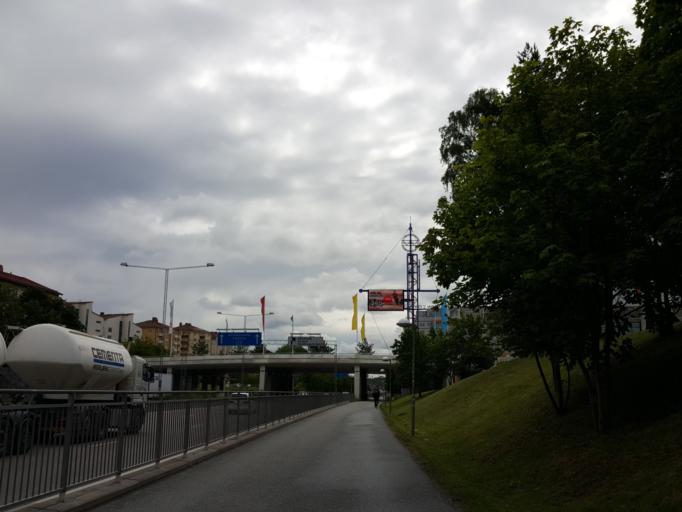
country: SE
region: Stockholm
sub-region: Stockholms Kommun
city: Arsta
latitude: 59.2955
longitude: 18.0842
